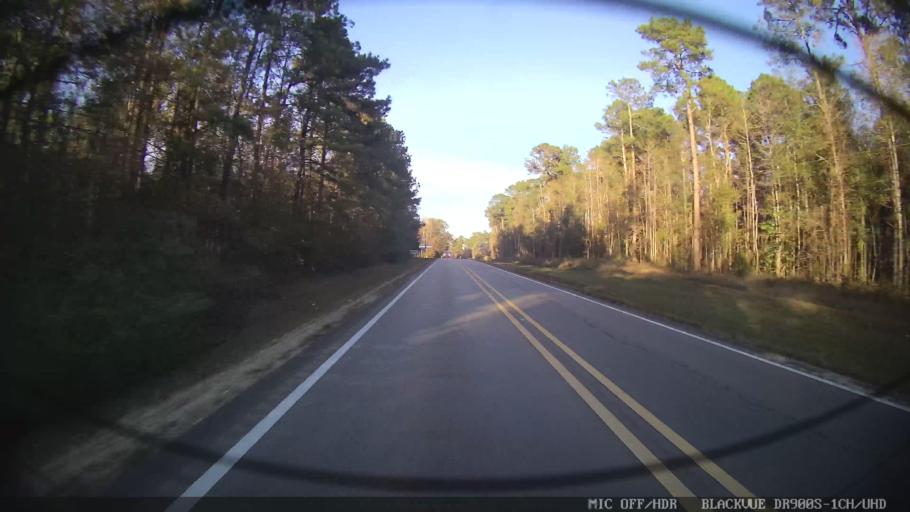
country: US
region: Mississippi
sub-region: Lamar County
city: Lumberton
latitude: 31.0313
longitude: -89.4440
